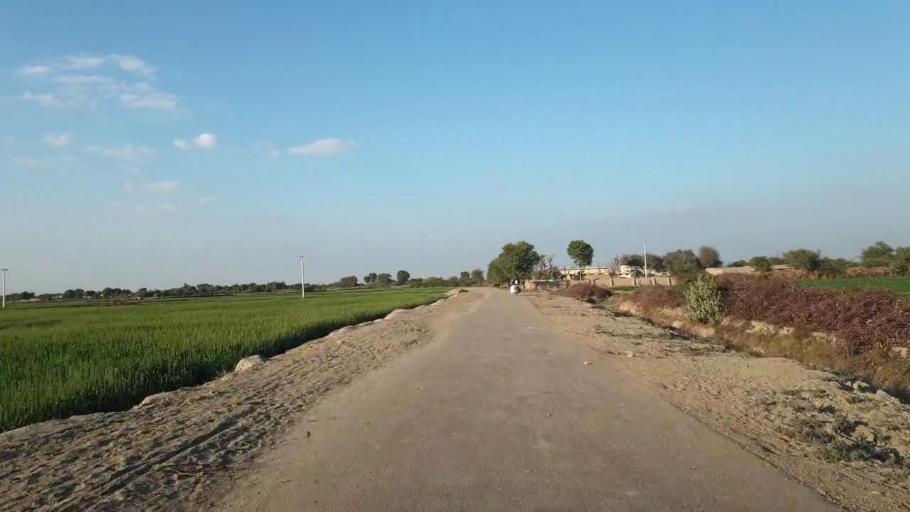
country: PK
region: Sindh
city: Shahpur Chakar
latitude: 26.1475
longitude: 68.5462
